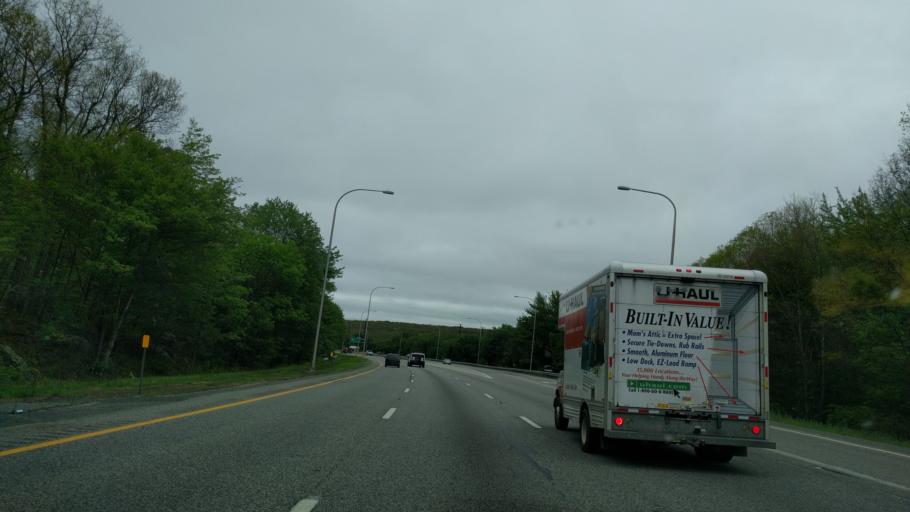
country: US
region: Rhode Island
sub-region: Providence County
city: Johnston
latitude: 41.8372
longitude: -71.5179
